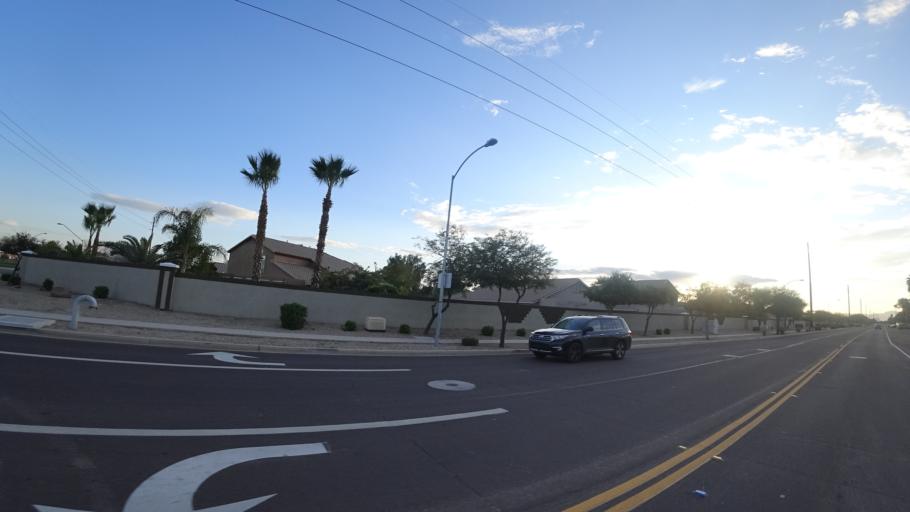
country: US
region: Arizona
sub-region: Maricopa County
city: Glendale
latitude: 33.5452
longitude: -112.2207
